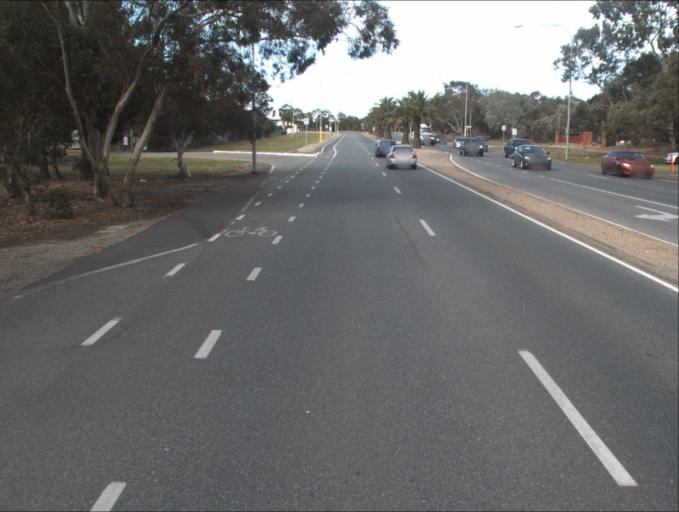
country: AU
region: South Australia
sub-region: Charles Sturt
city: West Lakes Shore
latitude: -34.8549
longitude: 138.5024
